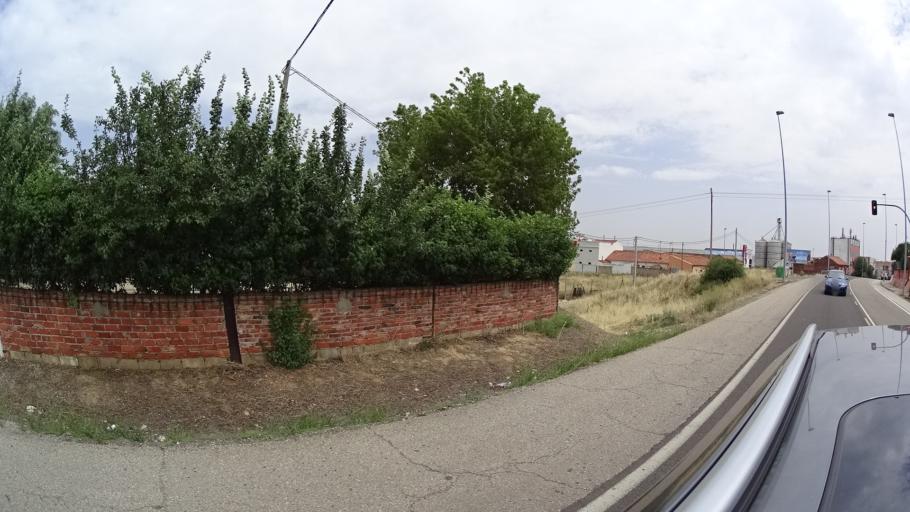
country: ES
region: Castille and Leon
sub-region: Provincia de Leon
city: Leon
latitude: 42.6157
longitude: -5.5787
